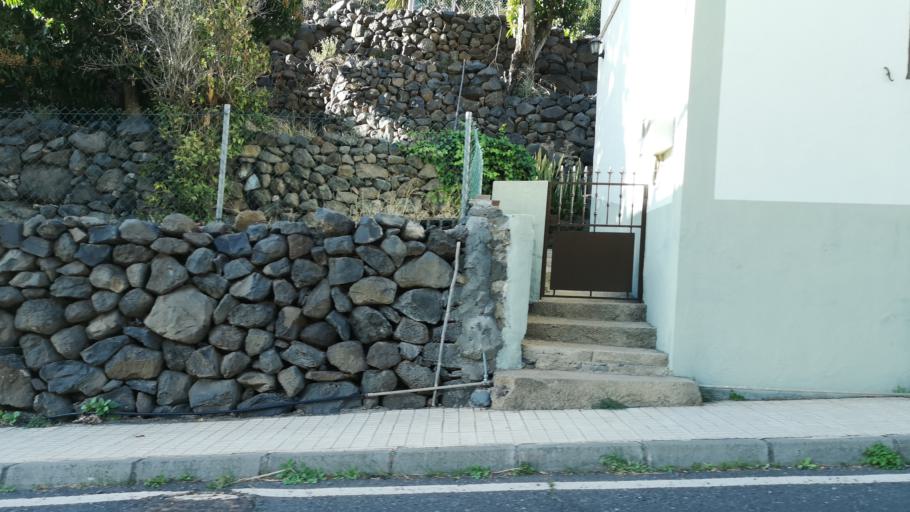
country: ES
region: Canary Islands
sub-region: Provincia de Santa Cruz de Tenerife
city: Vallehermosa
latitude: 28.1051
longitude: -17.3269
